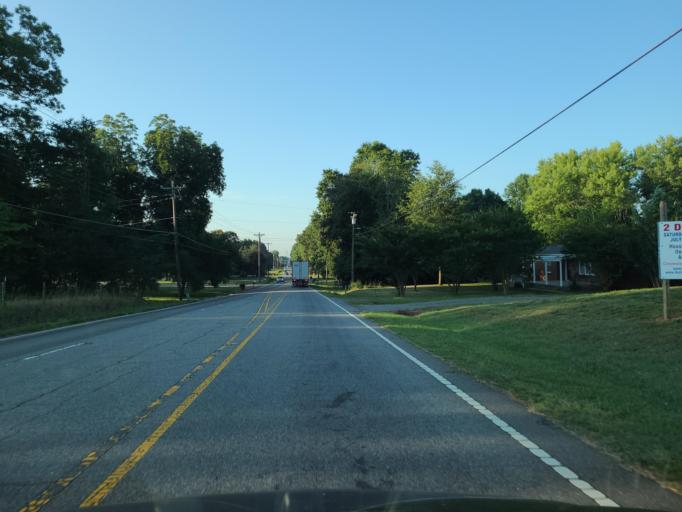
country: US
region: North Carolina
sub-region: Catawba County
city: Mountain View
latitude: 35.6708
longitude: -81.3843
